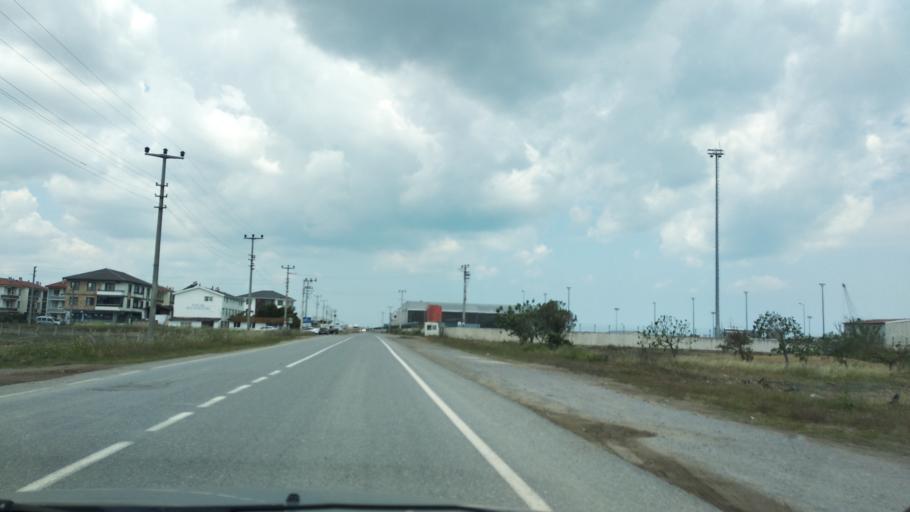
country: TR
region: Sakarya
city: Karasu
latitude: 41.1159
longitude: 30.6772
